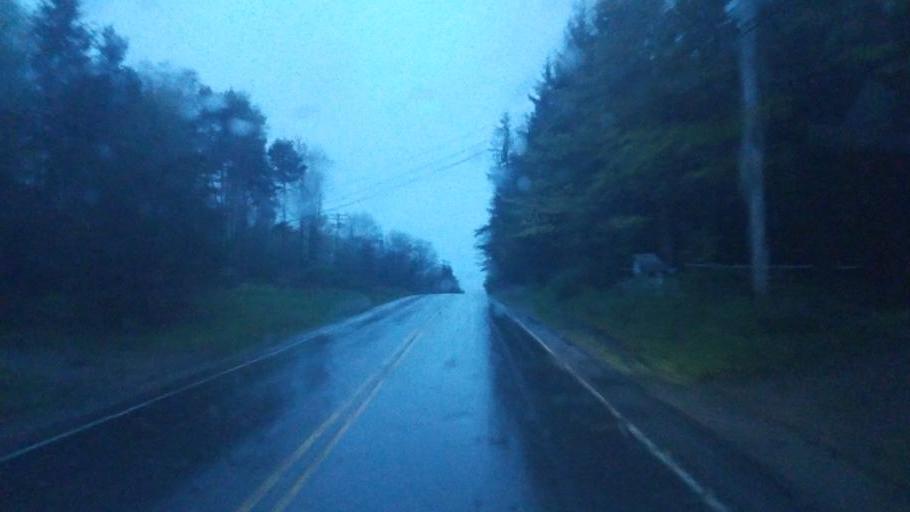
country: US
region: Pennsylvania
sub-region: Potter County
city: Galeton
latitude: 41.9126
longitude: -77.7556
